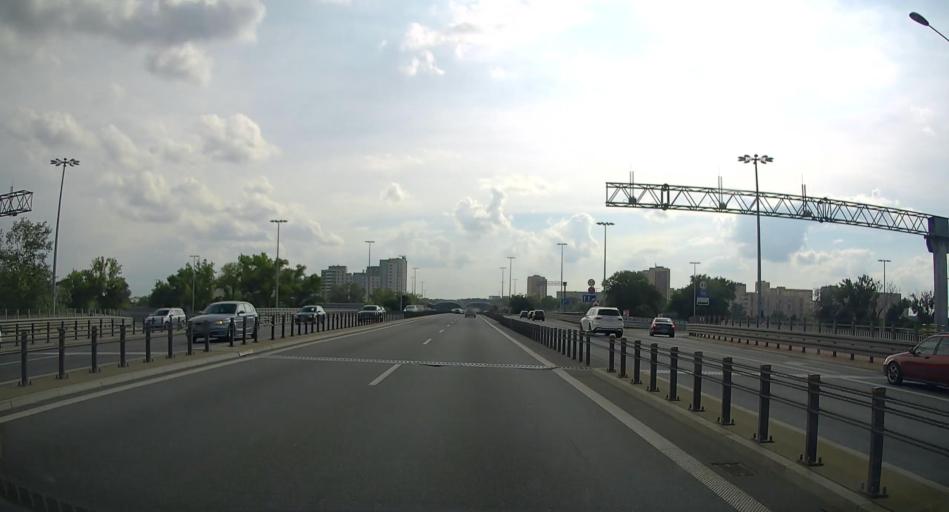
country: PL
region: Masovian Voivodeship
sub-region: Warszawa
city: Zoliborz
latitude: 52.2870
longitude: 20.9918
